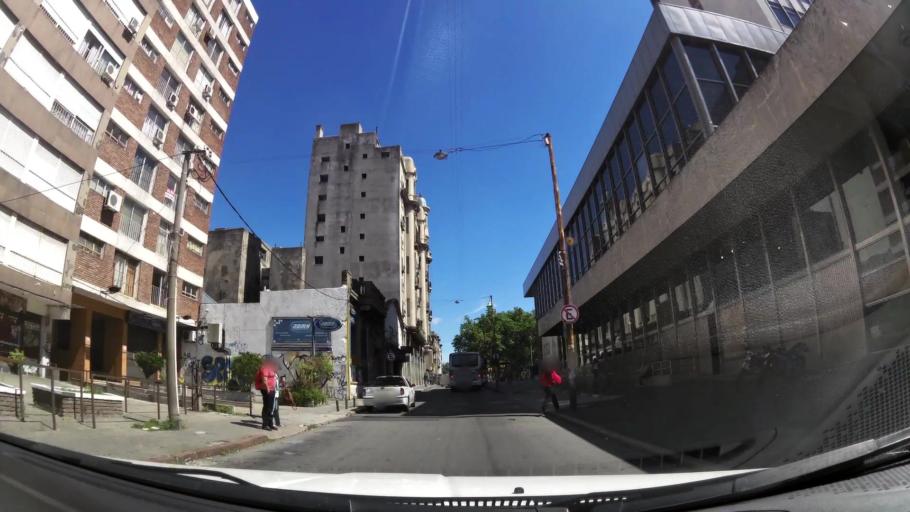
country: UY
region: Montevideo
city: Montevideo
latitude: -34.9044
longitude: -56.1801
